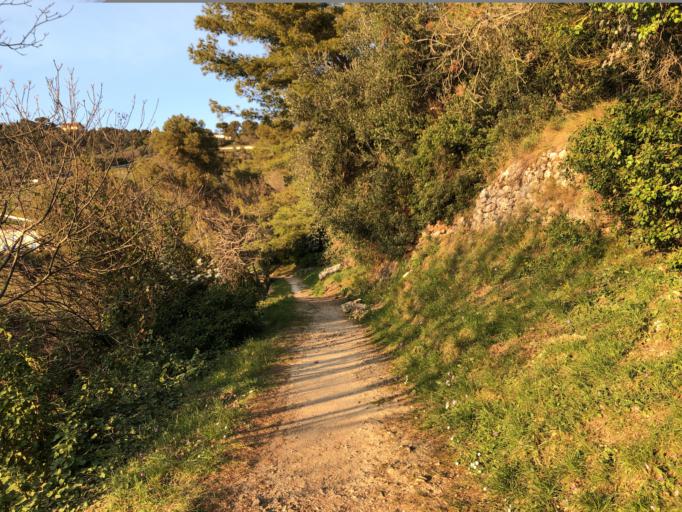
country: FR
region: Provence-Alpes-Cote d'Azur
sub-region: Departement des Alpes-Maritimes
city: Villefranche-sur-Mer
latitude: 43.7166
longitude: 7.3000
